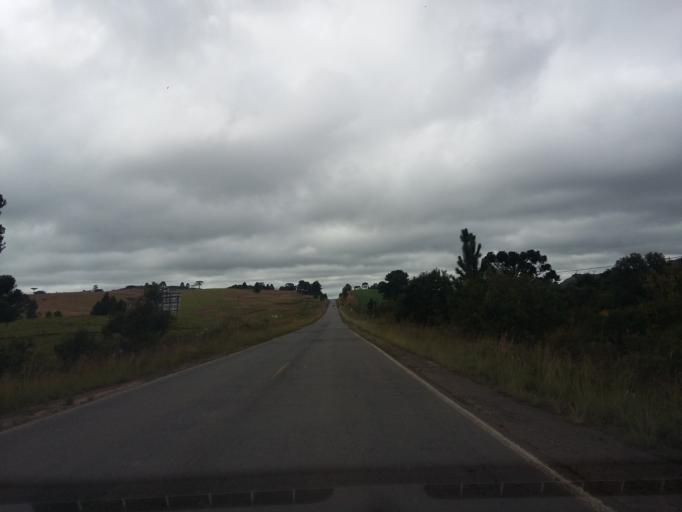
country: BR
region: Santa Catarina
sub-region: Lages
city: Lages
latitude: -27.8399
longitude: -50.2333
